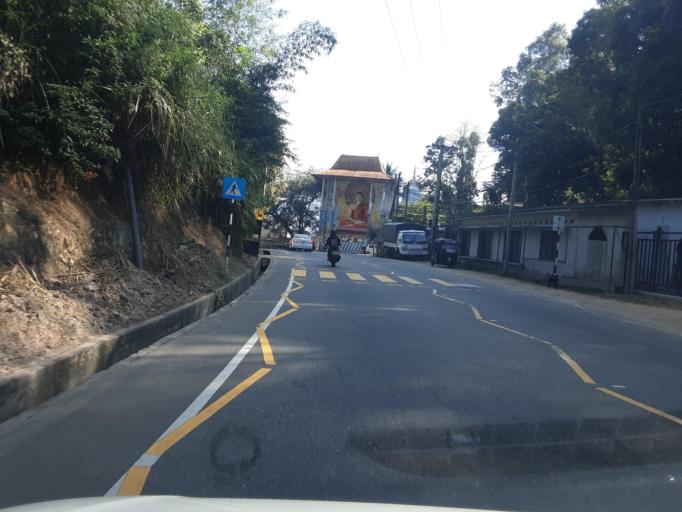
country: LK
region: Uva
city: Badulla
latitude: 6.9831
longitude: 81.0451
